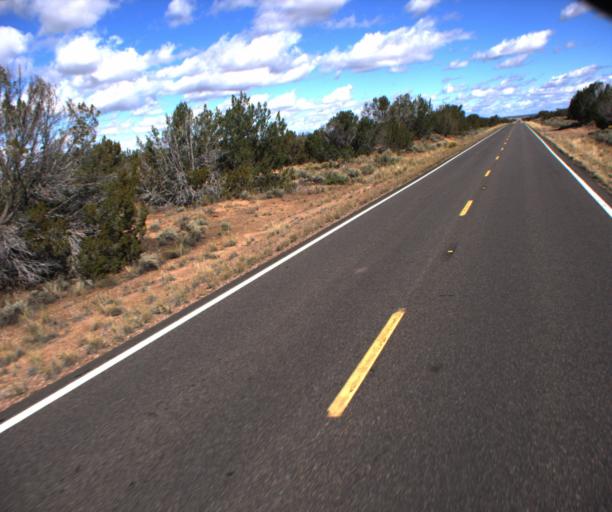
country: US
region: Arizona
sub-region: Apache County
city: Saint Johns
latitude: 34.8673
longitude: -109.2378
